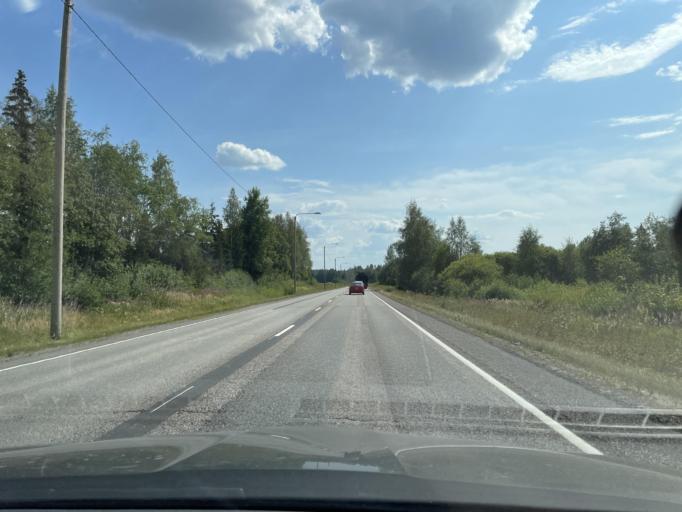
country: FI
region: Central Finland
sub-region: Jyvaeskylae
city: Korpilahti
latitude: 62.0505
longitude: 25.6028
